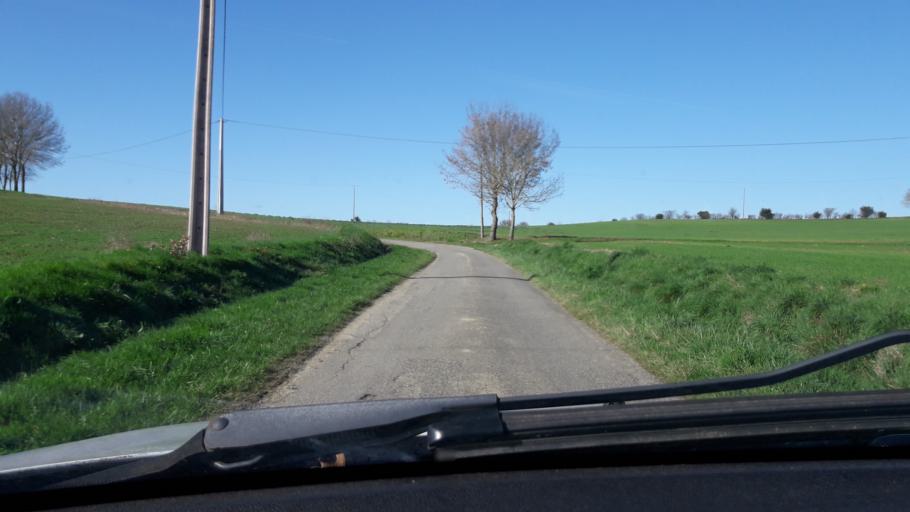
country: FR
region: Midi-Pyrenees
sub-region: Departement du Gers
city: Gimont
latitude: 43.6447
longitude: 1.0156
